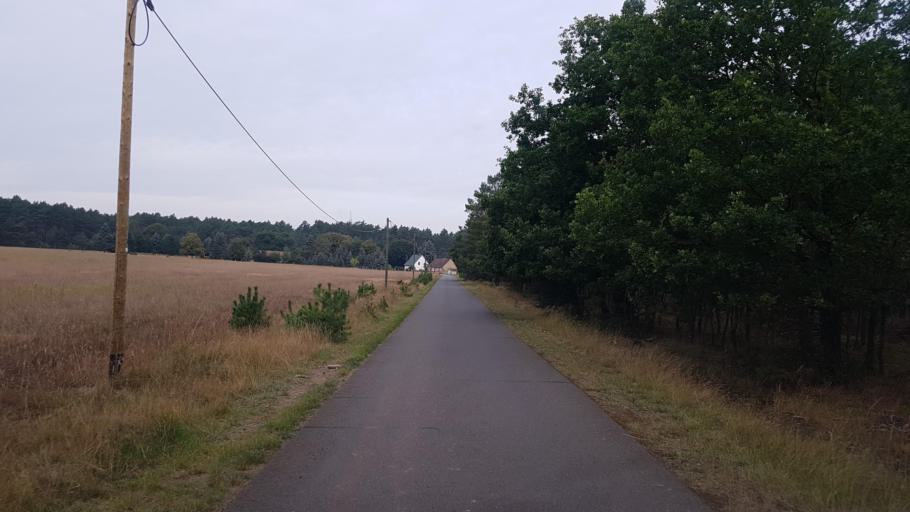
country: DE
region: Brandenburg
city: Schonewalde
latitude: 51.7868
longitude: 13.5821
